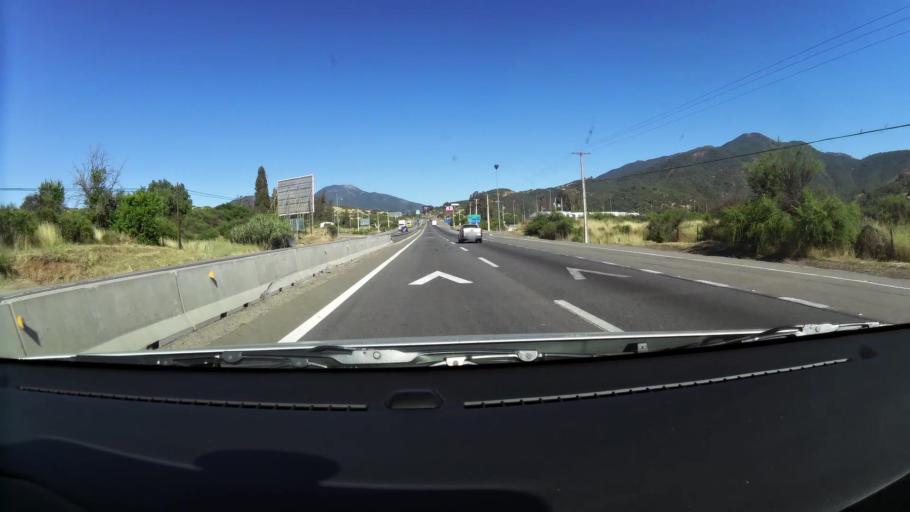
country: CL
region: Santiago Metropolitan
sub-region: Provincia de Melipilla
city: Melipilla
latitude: -33.4064
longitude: -71.1877
